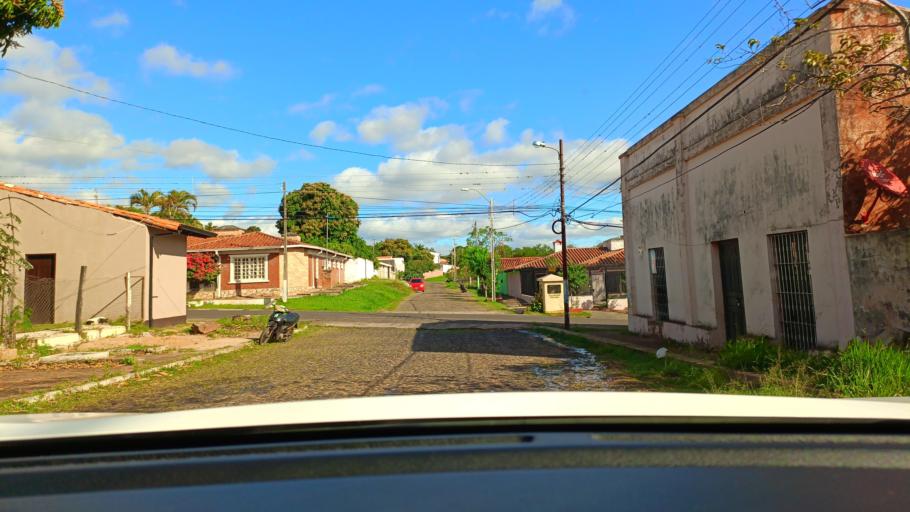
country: PY
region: San Pedro
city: Guayaybi
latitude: -24.6667
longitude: -56.4461
